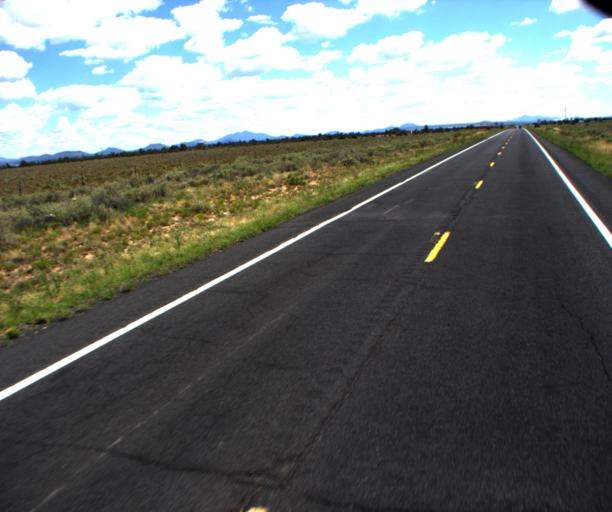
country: US
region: Arizona
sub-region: Coconino County
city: Grand Canyon Village
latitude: 35.6662
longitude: -112.1376
